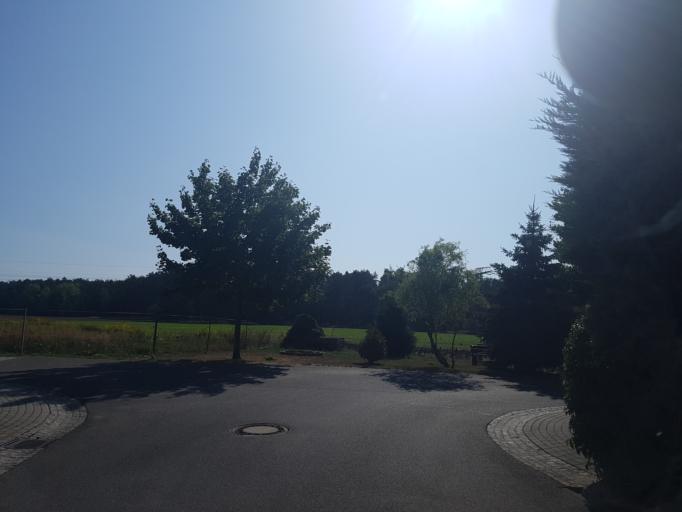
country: DE
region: Brandenburg
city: Finsterwalde
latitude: 51.6431
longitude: 13.7427
